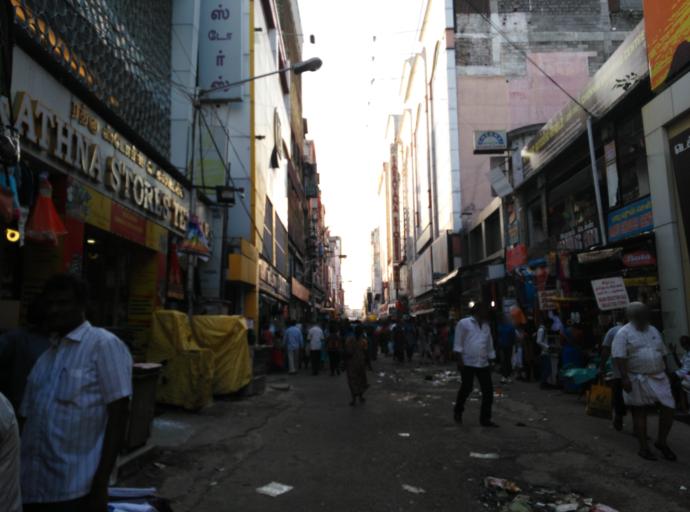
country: IN
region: Tamil Nadu
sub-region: Chennai
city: Chetput
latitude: 13.0369
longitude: 80.2301
